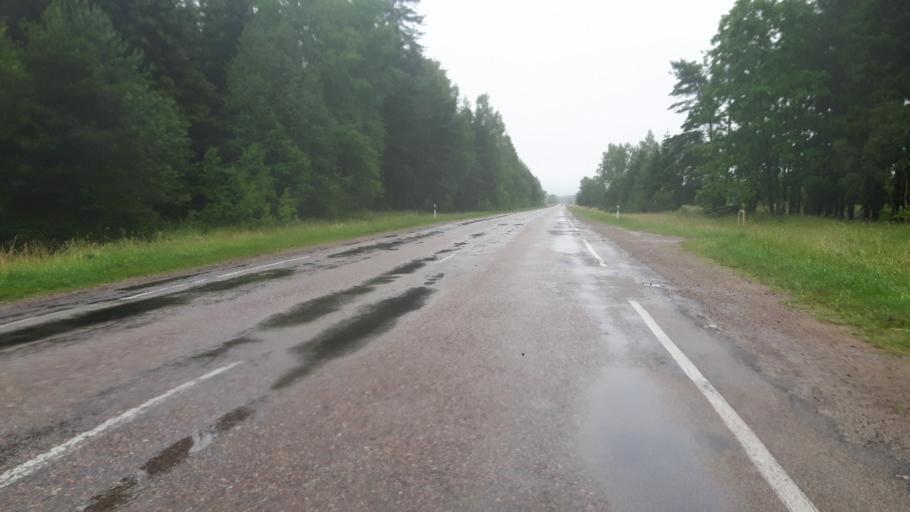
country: LT
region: Klaipedos apskritis
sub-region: Palanga
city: Sventoji
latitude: 56.0906
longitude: 21.1266
